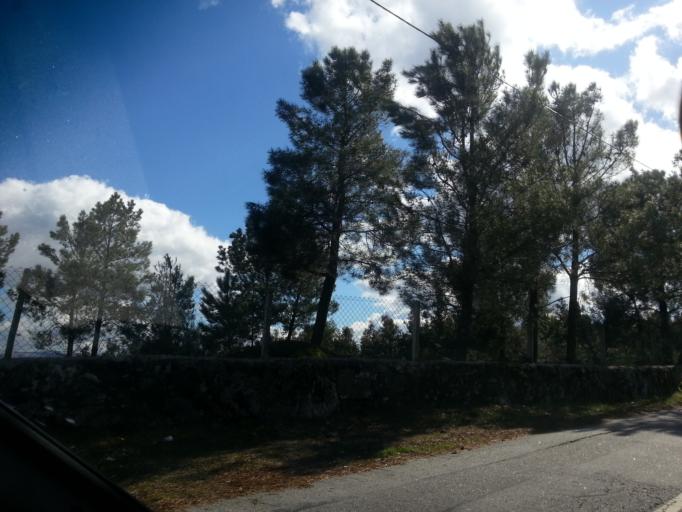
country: PT
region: Guarda
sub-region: Fornos de Algodres
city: Fornos de Algodres
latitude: 40.6435
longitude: -7.5232
